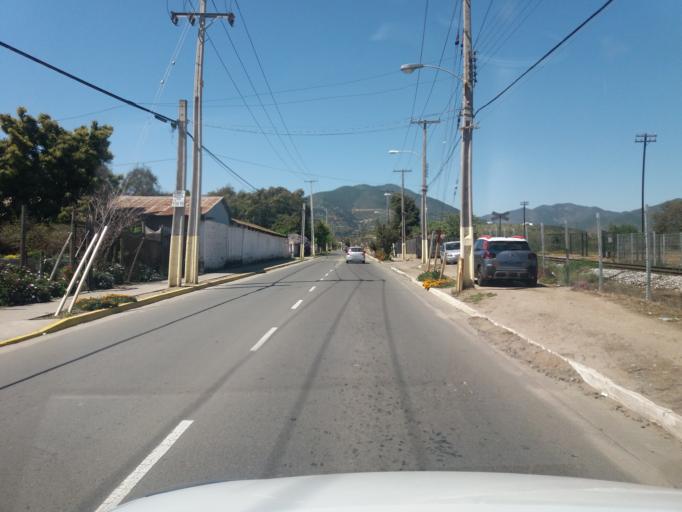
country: CL
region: Valparaiso
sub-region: Provincia de Quillota
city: Quillota
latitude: -32.9393
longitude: -71.2848
